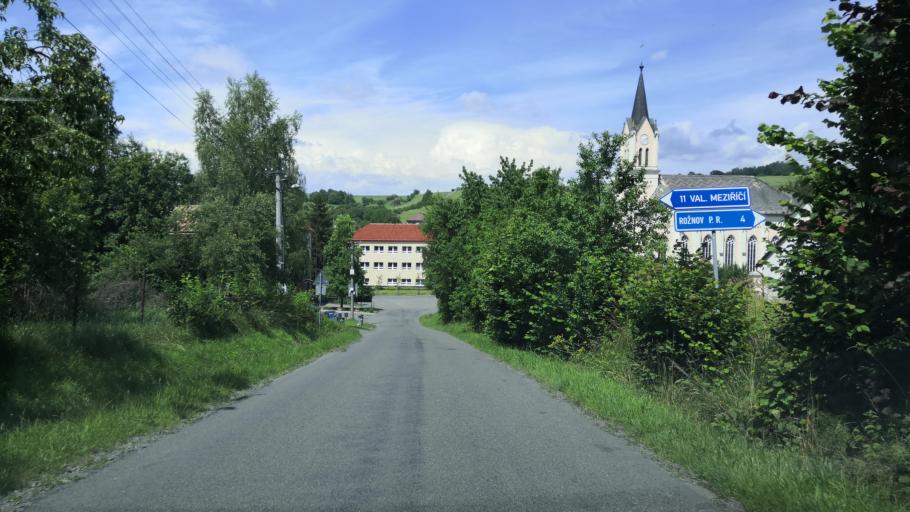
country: CZ
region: Zlin
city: Vidce
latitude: 49.4402
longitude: 18.0948
